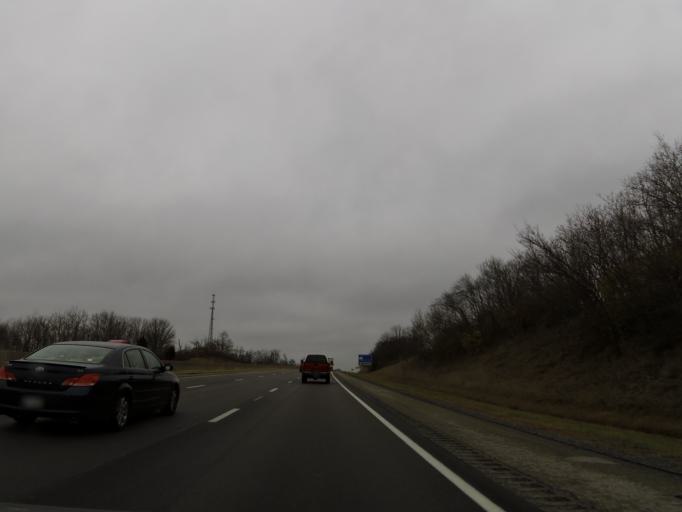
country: US
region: Kentucky
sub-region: Grant County
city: Dry Ridge
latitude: 38.7010
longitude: -84.6015
